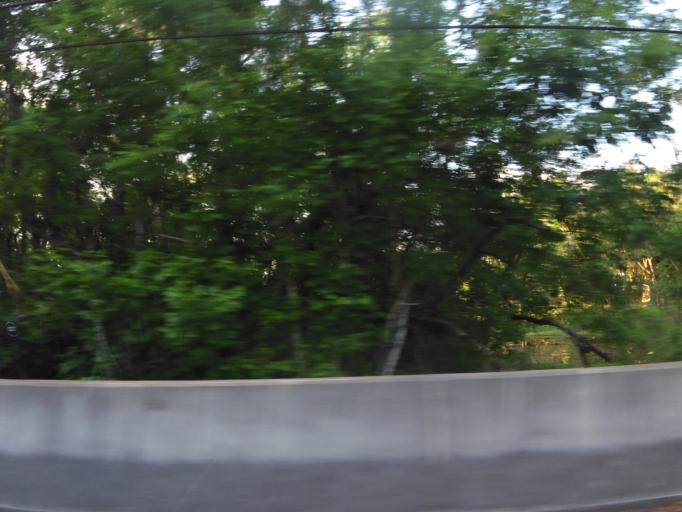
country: US
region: Florida
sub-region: Saint Johns County
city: Fruit Cove
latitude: 30.1276
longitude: -81.6040
